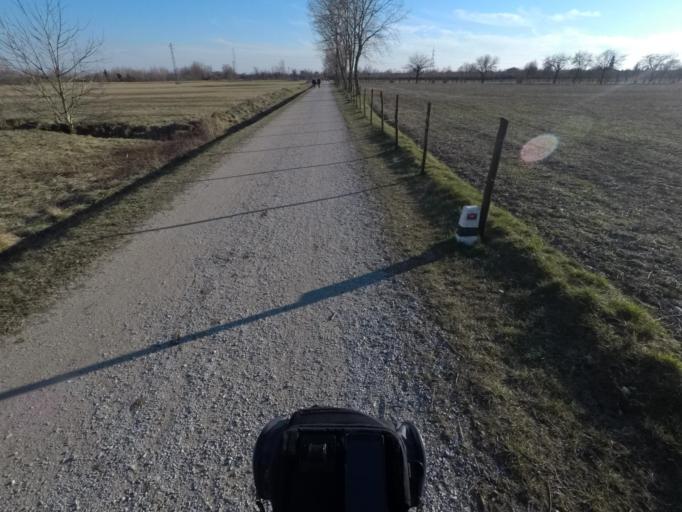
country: IT
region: Friuli Venezia Giulia
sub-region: Provincia di Udine
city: Povoletto
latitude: 46.1006
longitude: 13.2748
